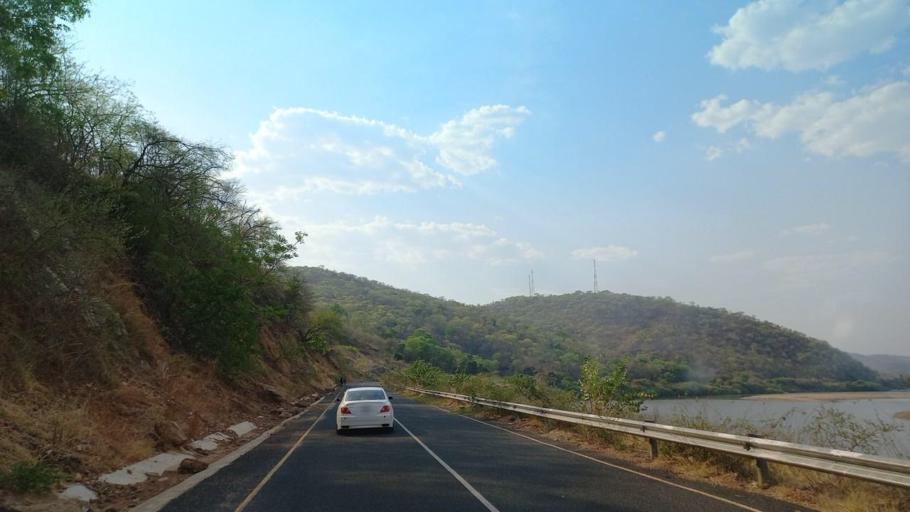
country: ZM
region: Lusaka
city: Luangwa
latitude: -15.0115
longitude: 30.2188
